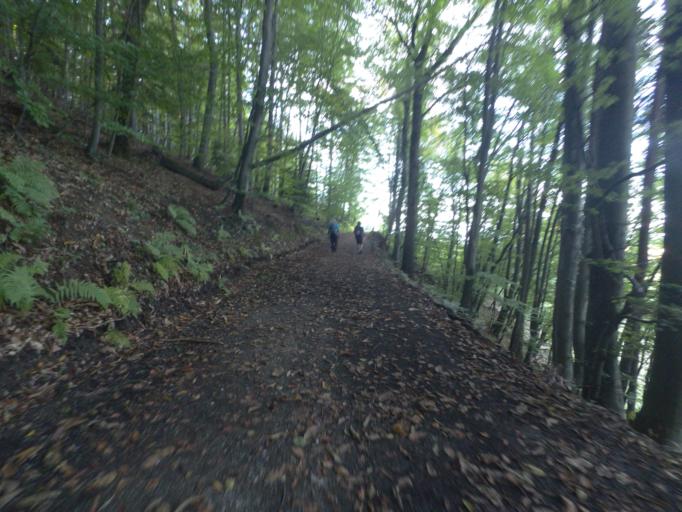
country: AT
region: Styria
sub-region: Politischer Bezirk Leibnitz
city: Kitzeck im Sausal
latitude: 46.7861
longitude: 15.4312
